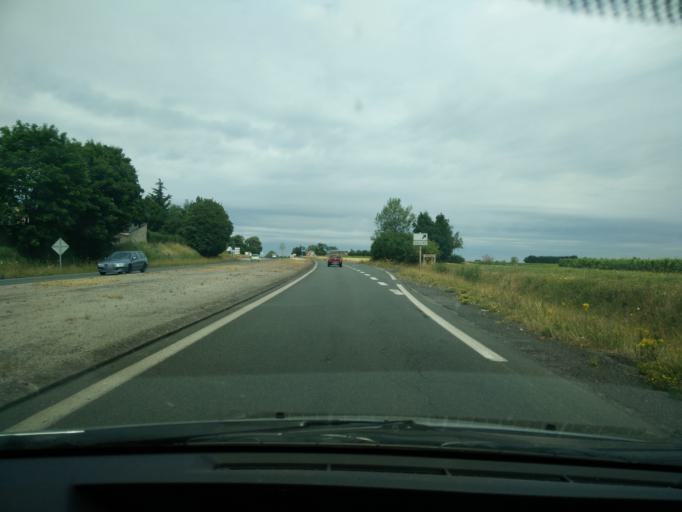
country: FR
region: Pays de la Loire
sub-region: Departement de Maine-et-Loire
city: Brissac-Quince
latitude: 47.3628
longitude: -0.4480
